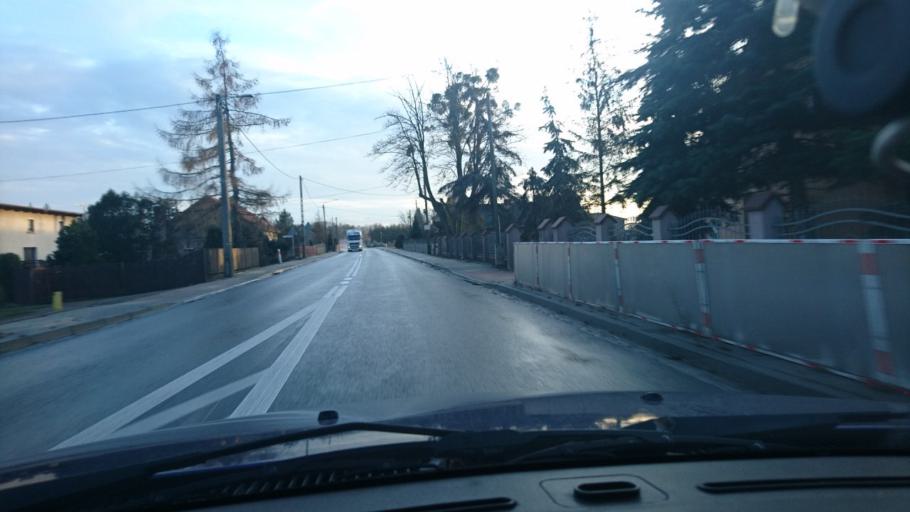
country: PL
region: Greater Poland Voivodeship
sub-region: Powiat kepinski
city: Opatow
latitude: 51.1698
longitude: 18.1466
